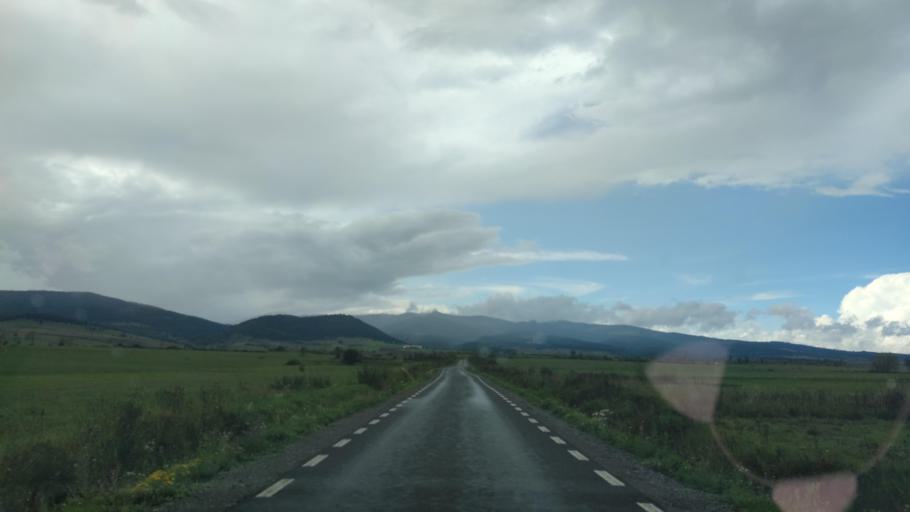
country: RO
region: Harghita
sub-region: Comuna Remetea
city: Remetea
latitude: 46.8073
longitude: 25.4144
